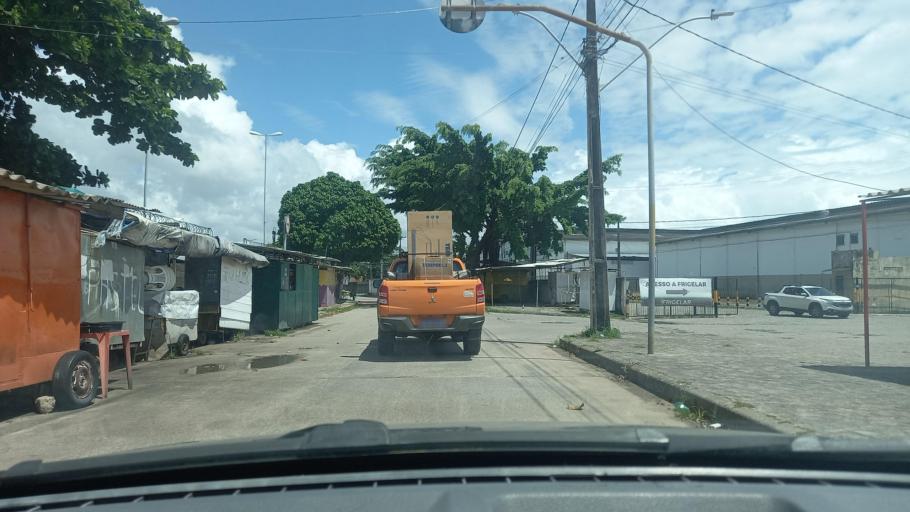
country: BR
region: Pernambuco
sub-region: Recife
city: Recife
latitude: -8.1037
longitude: -34.9092
